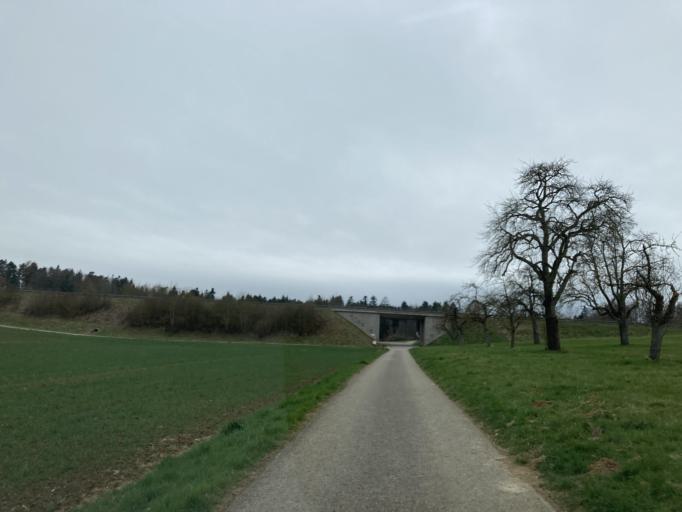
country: DE
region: Baden-Wuerttemberg
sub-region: Regierungsbezirk Stuttgart
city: Motzingen
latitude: 48.5154
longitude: 8.7785
